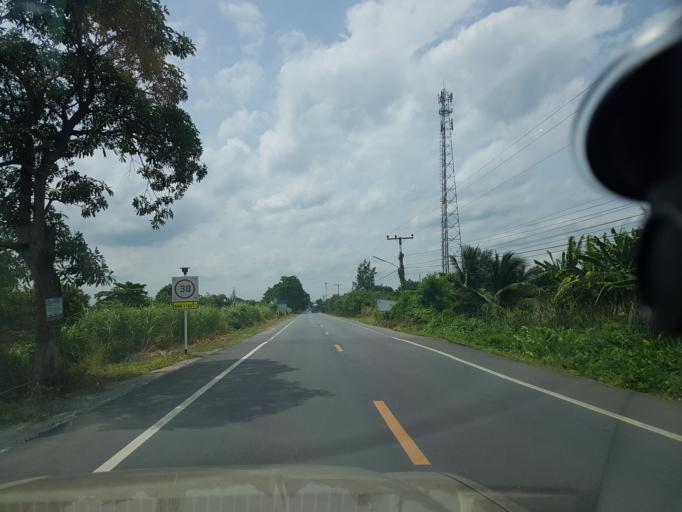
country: TH
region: Sara Buri
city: Nong Khae
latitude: 14.2410
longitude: 100.8919
